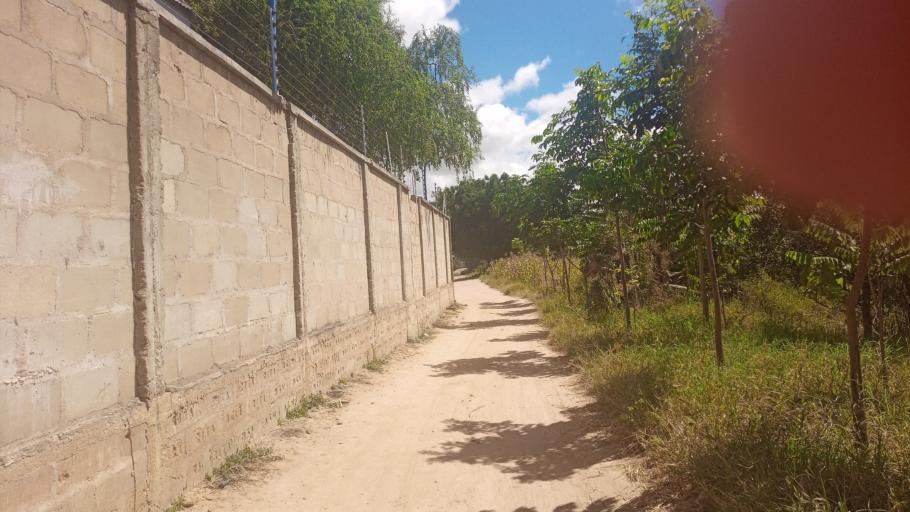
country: TZ
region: Dodoma
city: Dodoma
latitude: -6.1917
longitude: 35.7308
